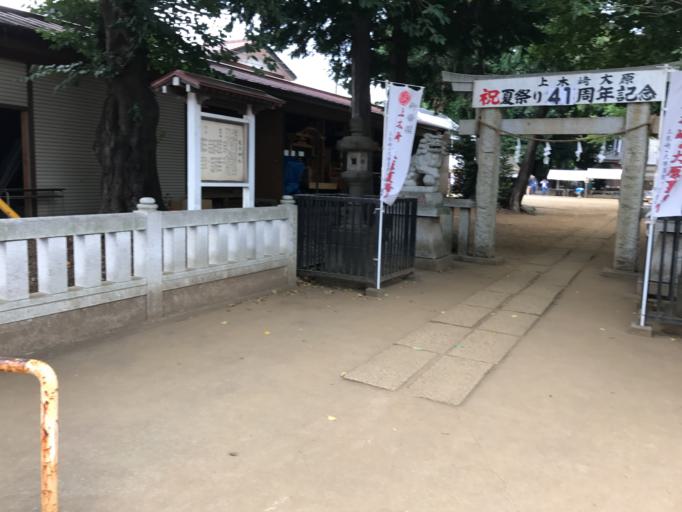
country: JP
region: Saitama
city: Yono
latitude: 35.8883
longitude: 139.6468
